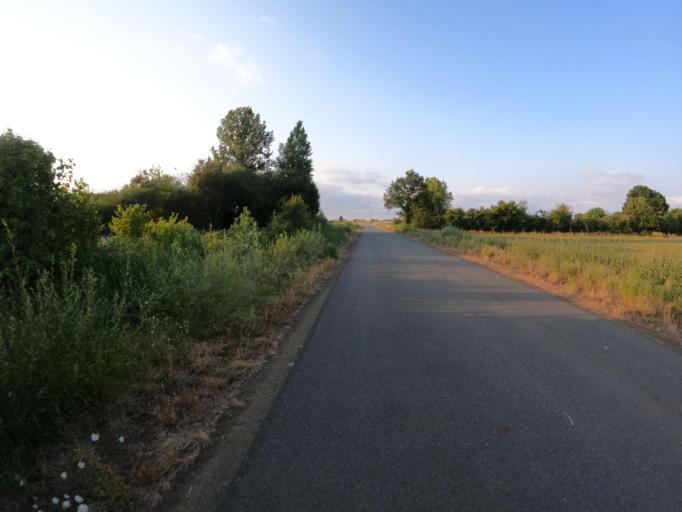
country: FR
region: Pays de la Loire
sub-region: Departement de la Sarthe
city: Brulon
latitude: 47.9127
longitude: -0.2288
